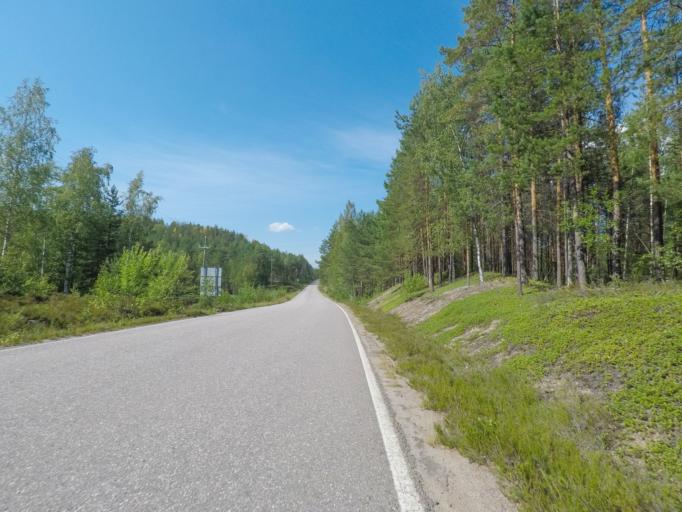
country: FI
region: Southern Savonia
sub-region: Mikkeli
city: Puumala
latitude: 61.4618
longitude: 28.1748
